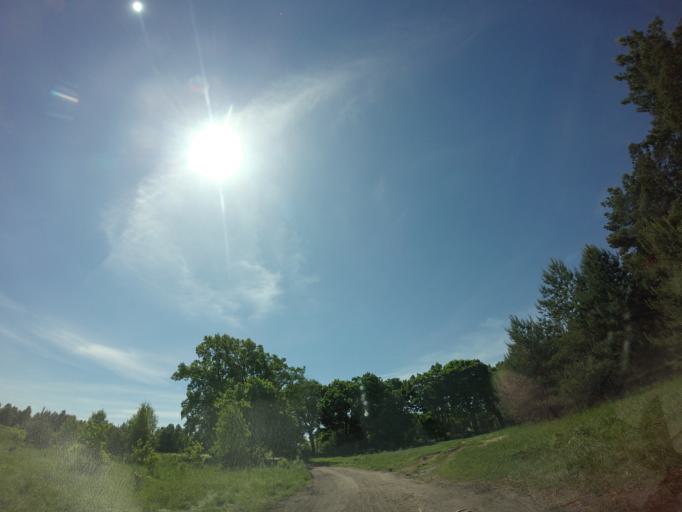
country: PL
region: West Pomeranian Voivodeship
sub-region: Powiat choszczenski
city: Drawno
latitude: 53.2889
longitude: 15.6843
